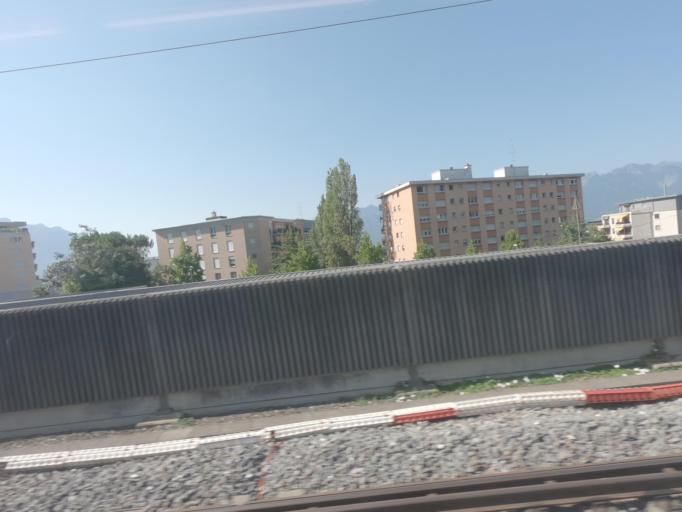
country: CH
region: Vaud
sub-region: Riviera-Pays-d'Enhaut District
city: Le Chatelard
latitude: 46.4439
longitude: 6.8887
